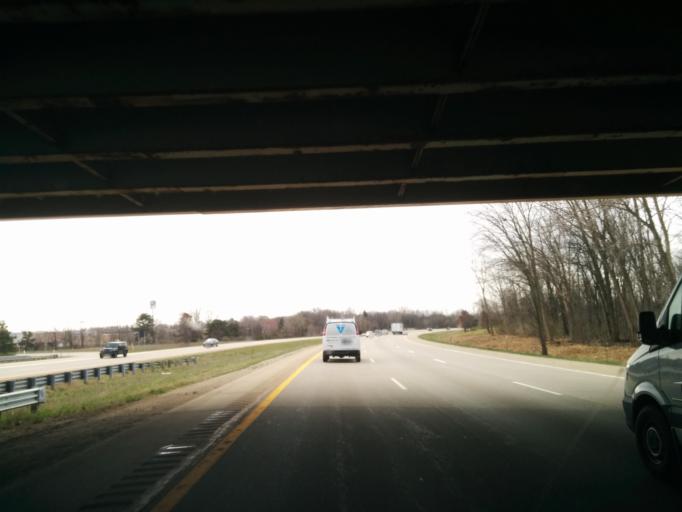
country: US
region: Michigan
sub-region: Ottawa County
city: Jenison
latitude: 42.8853
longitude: -85.7774
